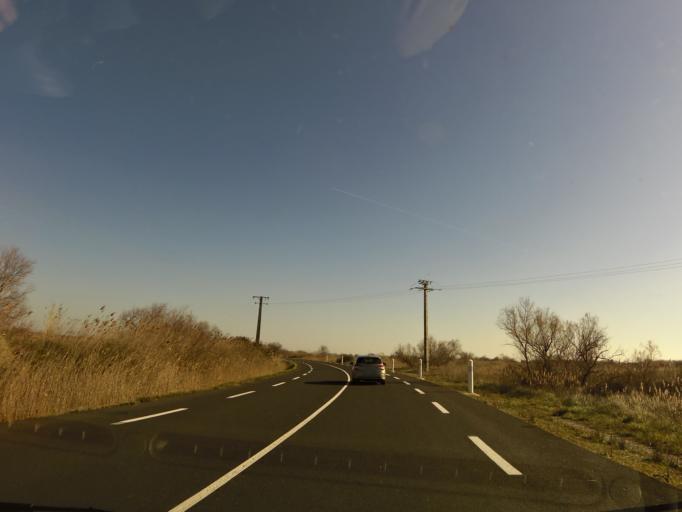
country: FR
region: Languedoc-Roussillon
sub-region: Departement du Gard
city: Aigues-Mortes
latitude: 43.5560
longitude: 4.3215
